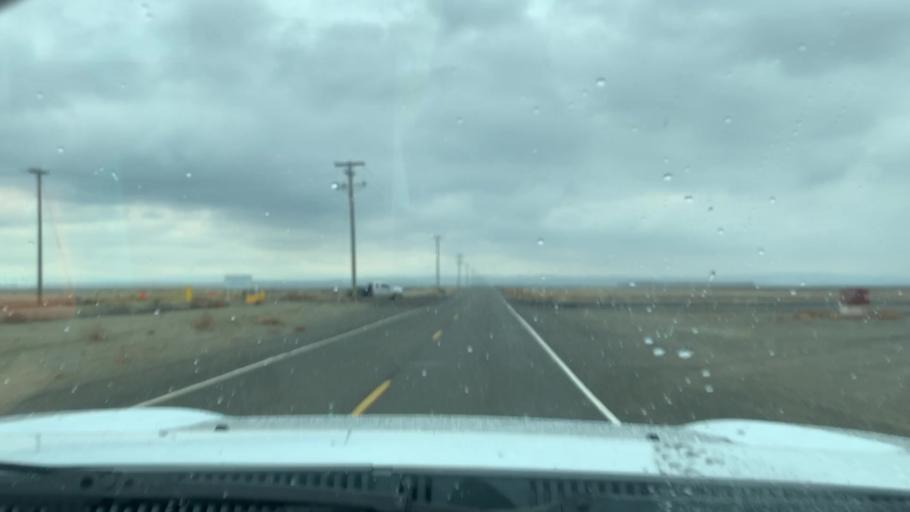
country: US
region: California
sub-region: Kings County
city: Kettleman City
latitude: 35.9341
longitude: -119.8426
